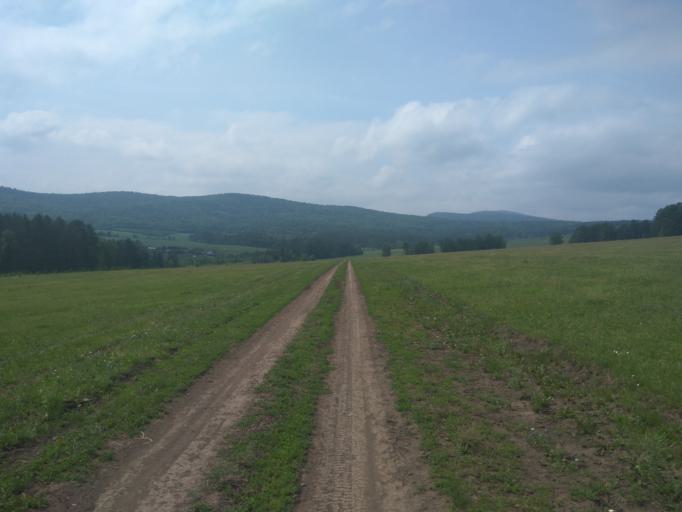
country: RU
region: Krasnoyarskiy
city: Zykovo
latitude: 55.8455
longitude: 93.2067
